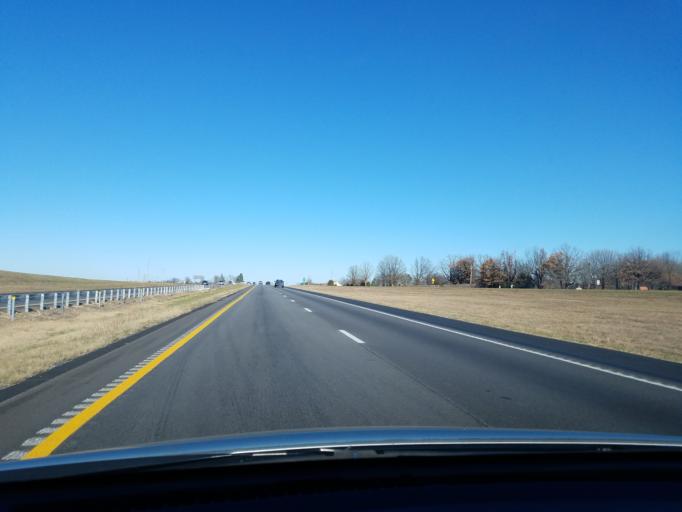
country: US
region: Missouri
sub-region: Webster County
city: Marshfield
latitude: 37.3834
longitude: -92.9025
